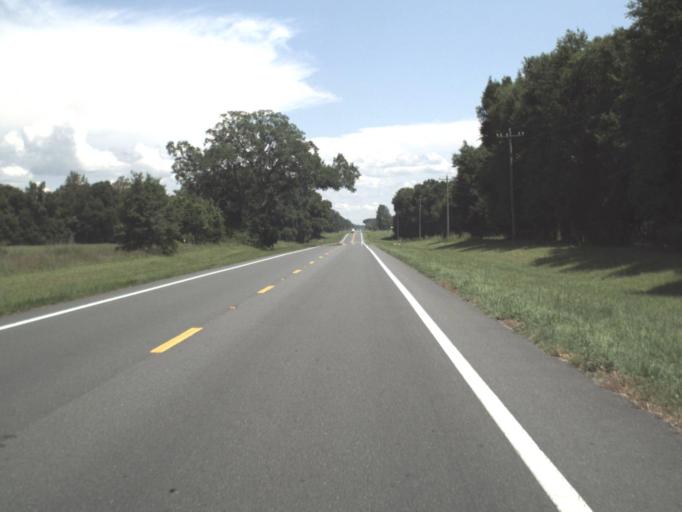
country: US
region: Florida
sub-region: Lafayette County
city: Mayo
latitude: 30.1030
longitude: -83.2435
